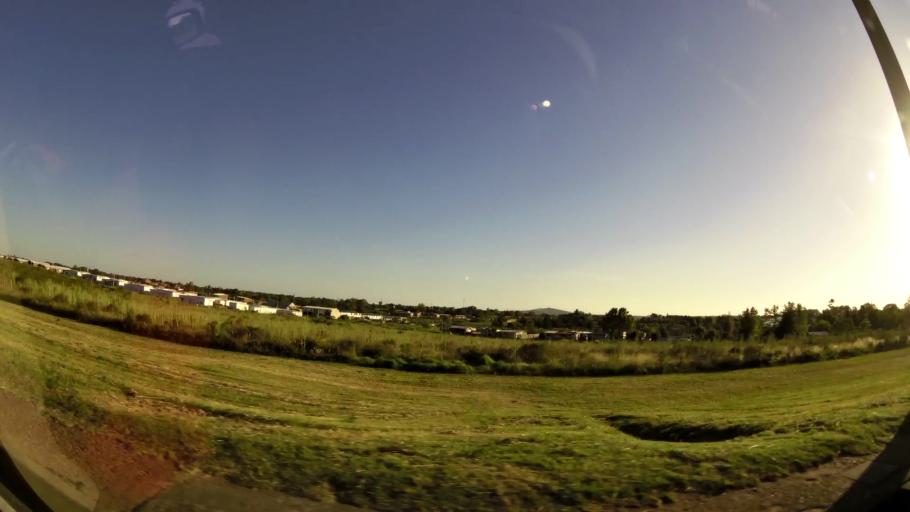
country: UY
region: Canelones
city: La Paz
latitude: -34.8278
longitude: -56.2368
